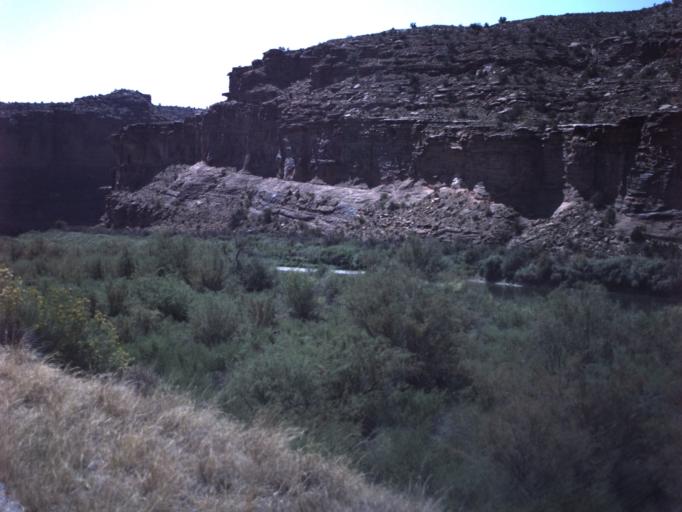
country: US
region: Utah
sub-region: Grand County
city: Moab
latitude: 38.8061
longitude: -109.3135
